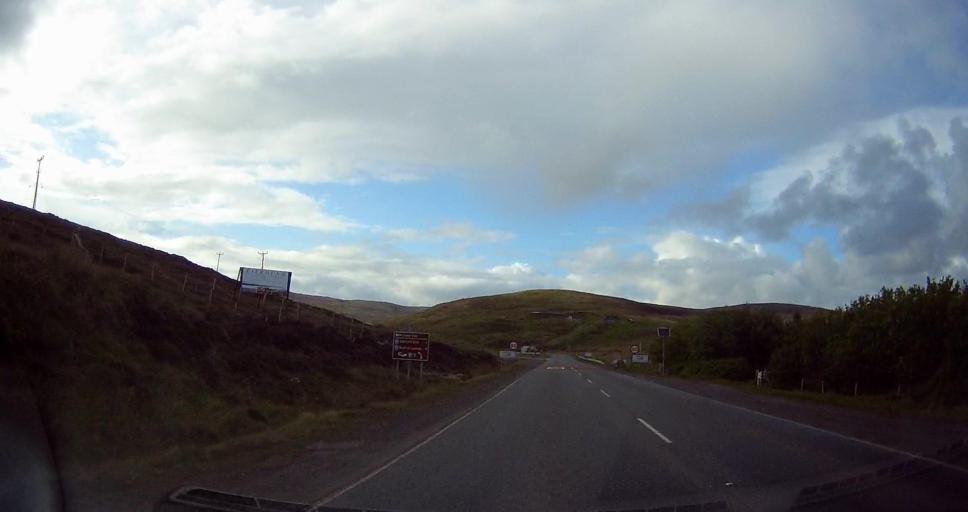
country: GB
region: Scotland
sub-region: Shetland Islands
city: Lerwick
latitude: 60.3470
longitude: -1.2533
